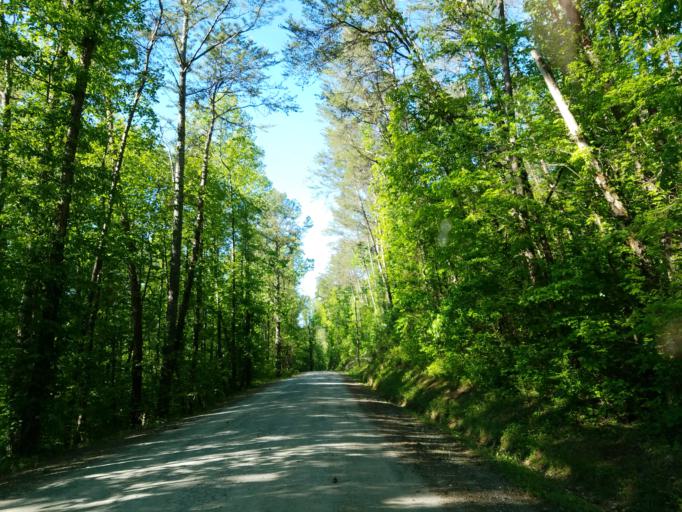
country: US
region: Georgia
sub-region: Gilmer County
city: Ellijay
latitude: 34.6125
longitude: -84.5040
